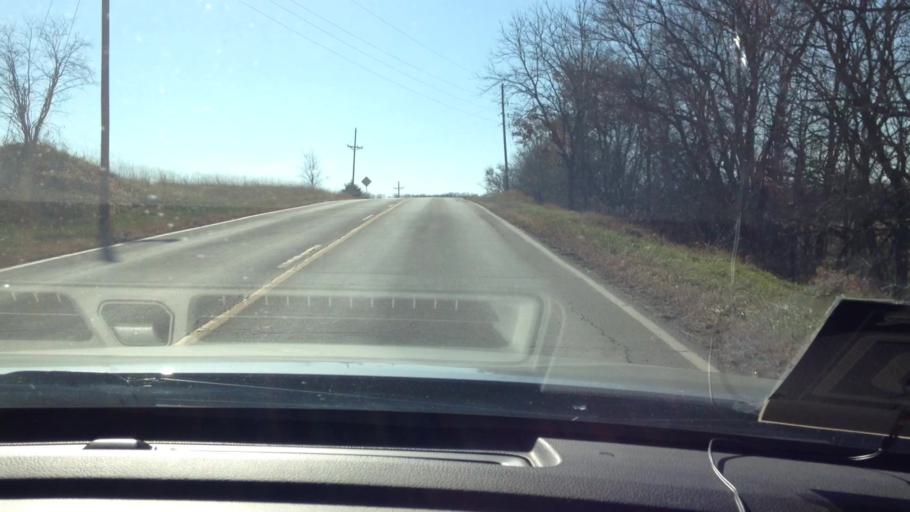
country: US
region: Missouri
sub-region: Platte County
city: Platte City
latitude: 39.4903
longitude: -94.8041
